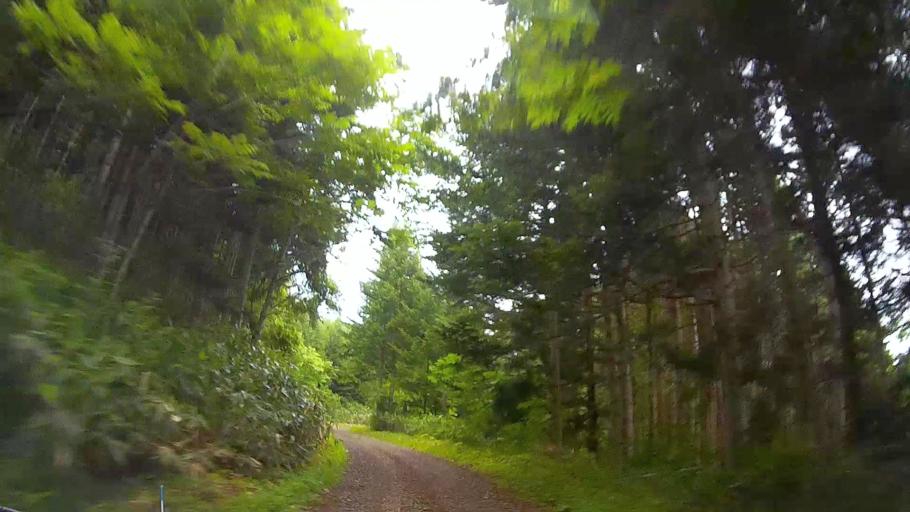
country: JP
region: Hokkaido
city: Nanae
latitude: 42.1243
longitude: 140.4256
